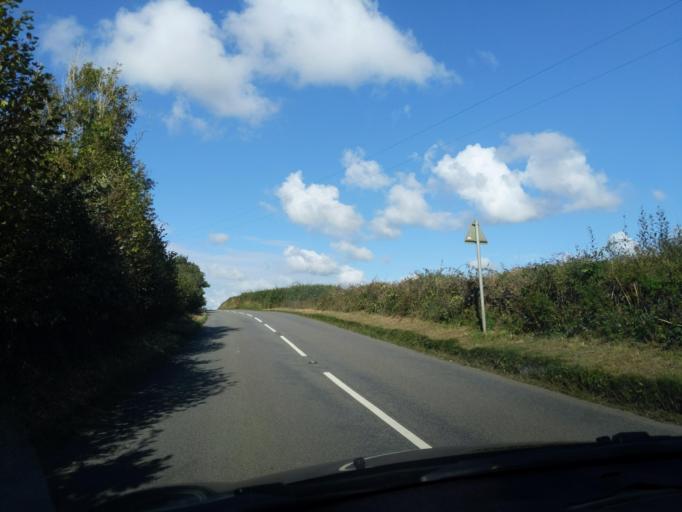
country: GB
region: England
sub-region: Devon
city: Holsworthy
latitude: 50.7777
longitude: -4.3349
